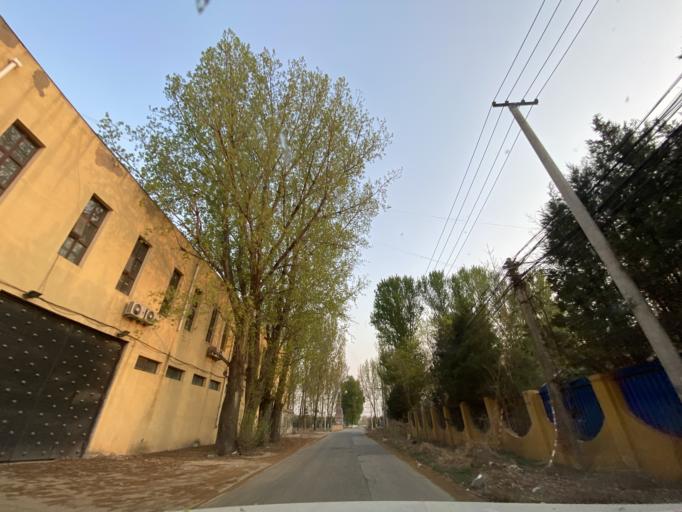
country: CN
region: Beijing
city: Weishanzhuang
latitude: 39.6074
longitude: 116.4218
